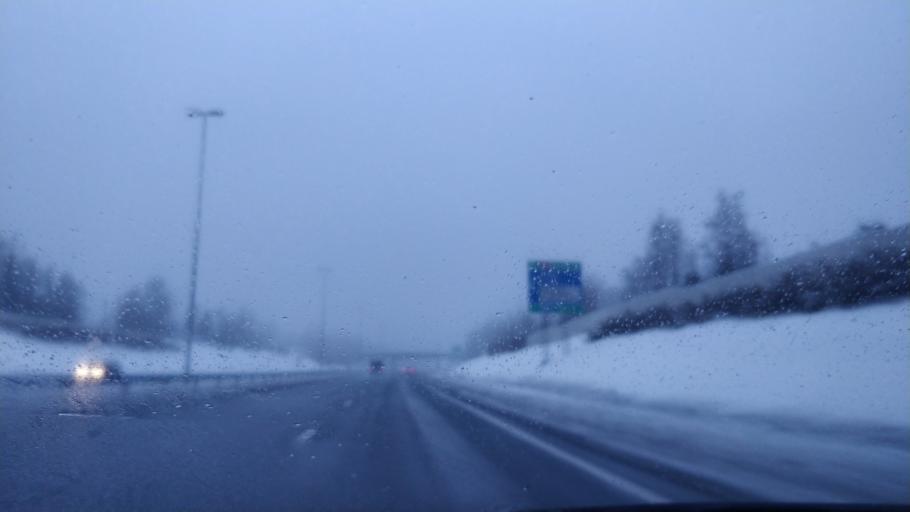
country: FI
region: Lapland
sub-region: Kemi-Tornio
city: Kemi
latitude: 65.7483
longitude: 24.5776
